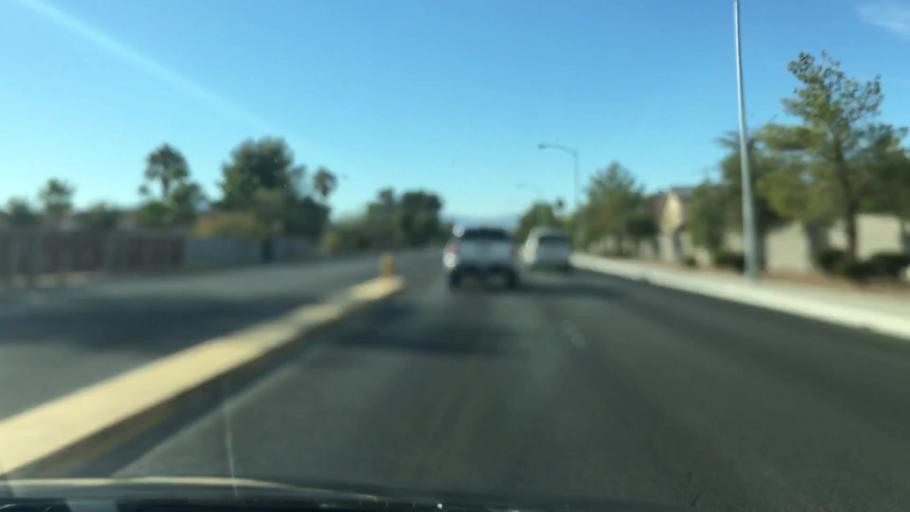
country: US
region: Nevada
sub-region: Clark County
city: Whitney
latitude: 36.0496
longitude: -115.1194
